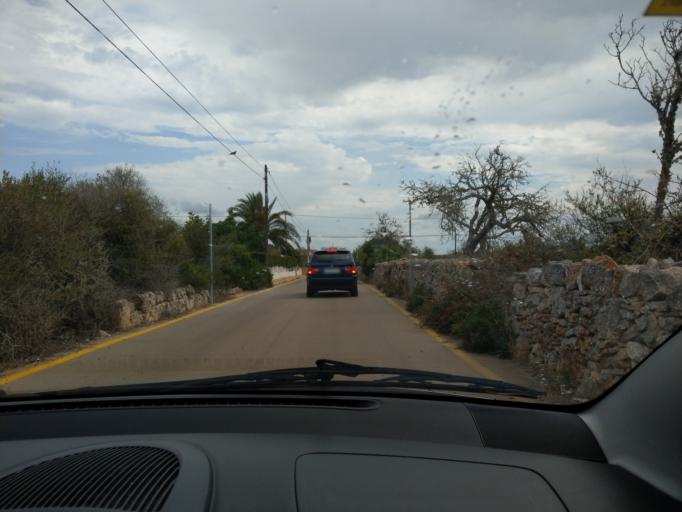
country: ES
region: Balearic Islands
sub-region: Illes Balears
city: Santanyi
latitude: 39.3203
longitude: 3.1251
